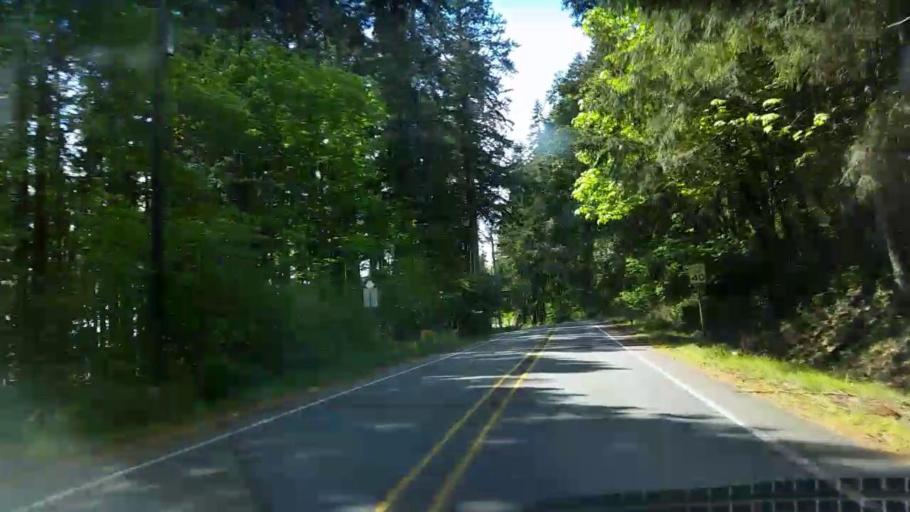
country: US
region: Washington
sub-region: Mason County
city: Allyn
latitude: 47.3618
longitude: -122.7935
